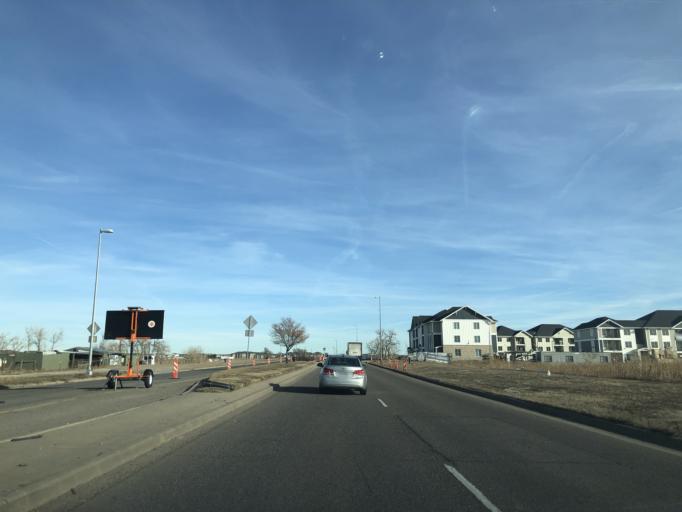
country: US
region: Colorado
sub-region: Adams County
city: Aurora
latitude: 39.7981
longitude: -104.7806
